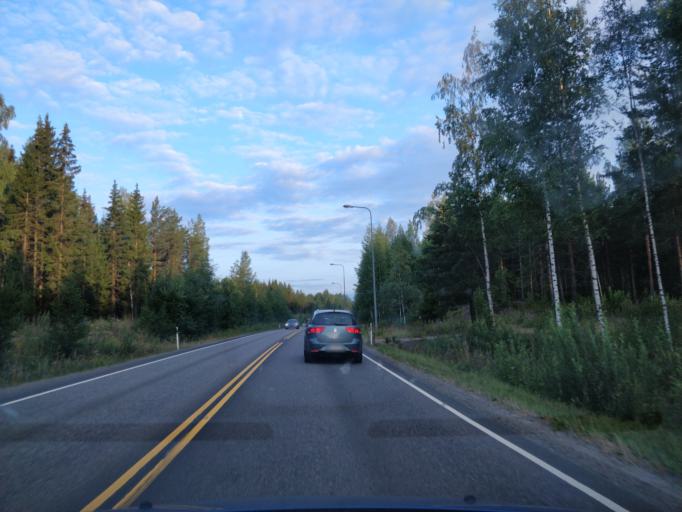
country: FI
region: Uusimaa
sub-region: Helsinki
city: Kerava
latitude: 60.3837
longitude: 25.1583
